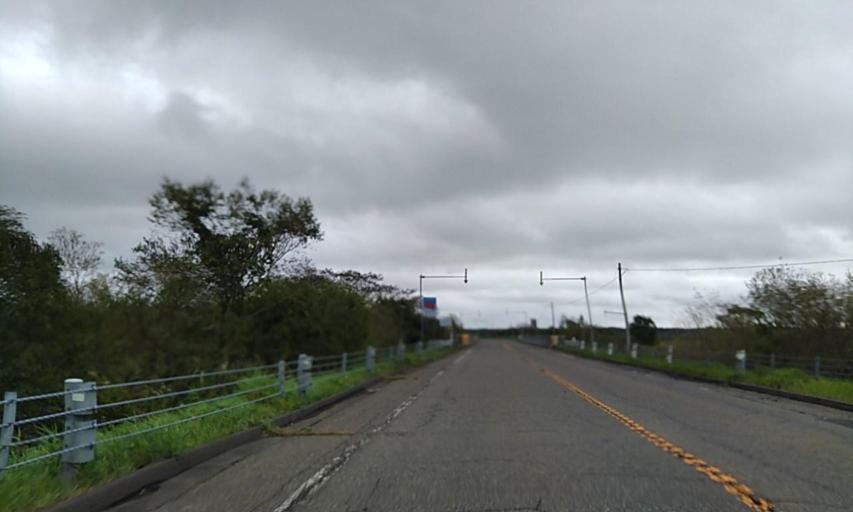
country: JP
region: Hokkaido
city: Nemuro
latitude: 43.2770
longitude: 145.2272
